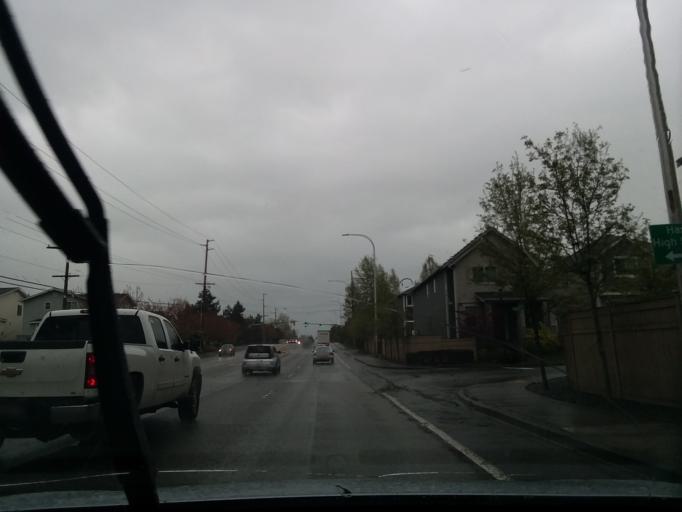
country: US
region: Washington
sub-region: King County
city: Fairwood
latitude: 47.4884
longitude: -122.1535
